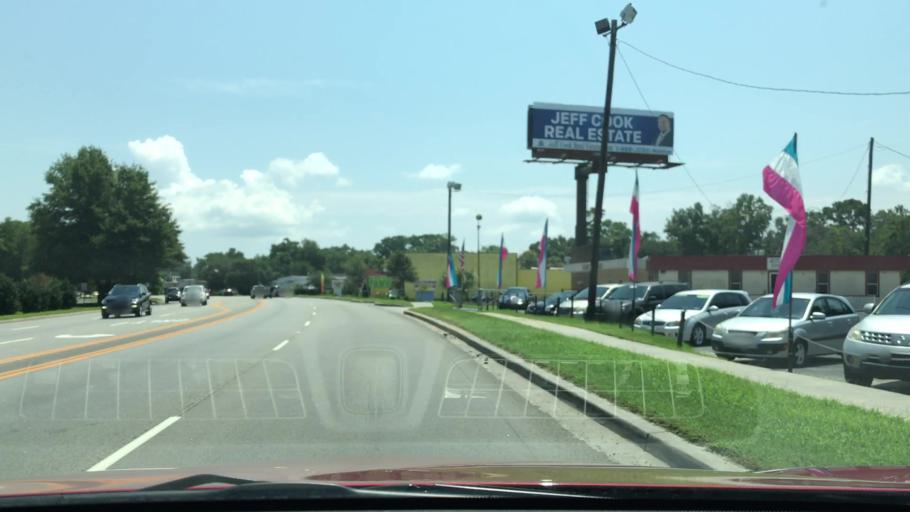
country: US
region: South Carolina
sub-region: Berkeley County
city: Hanahan
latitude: 32.8563
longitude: -80.0424
